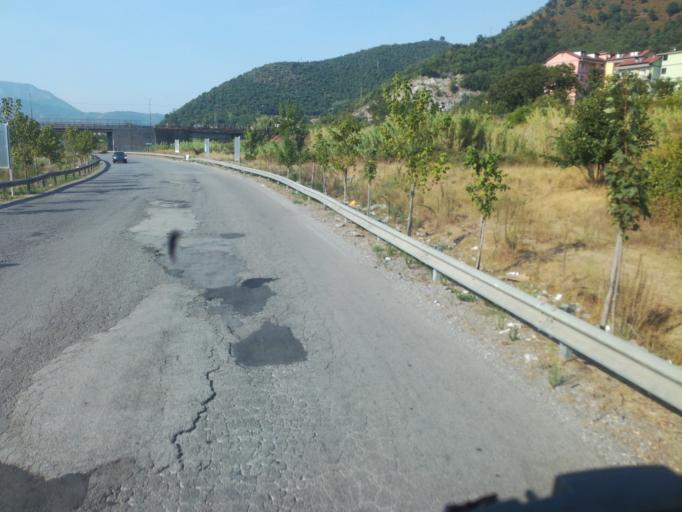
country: IT
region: Campania
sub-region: Provincia di Salerno
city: Piazza di Pandola
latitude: 40.7955
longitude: 14.7714
